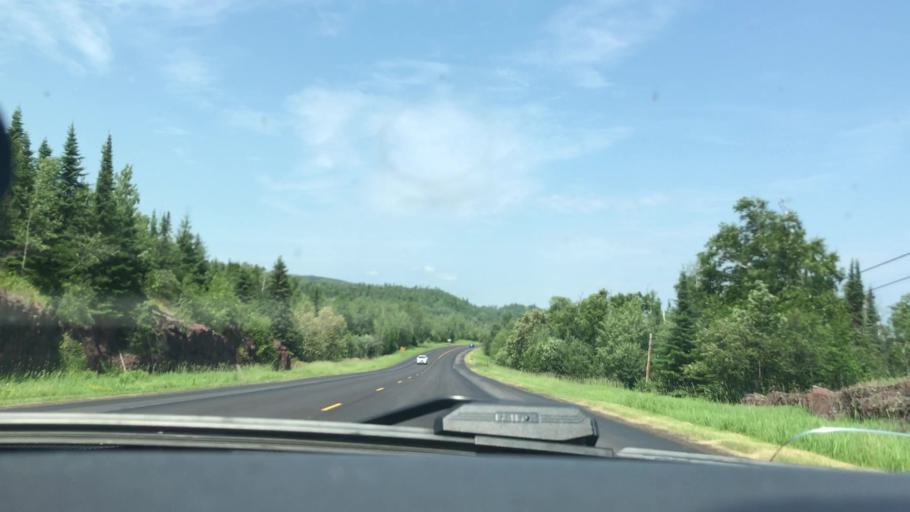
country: US
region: Minnesota
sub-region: Lake County
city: Silver Bay
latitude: 47.3521
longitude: -91.1828
